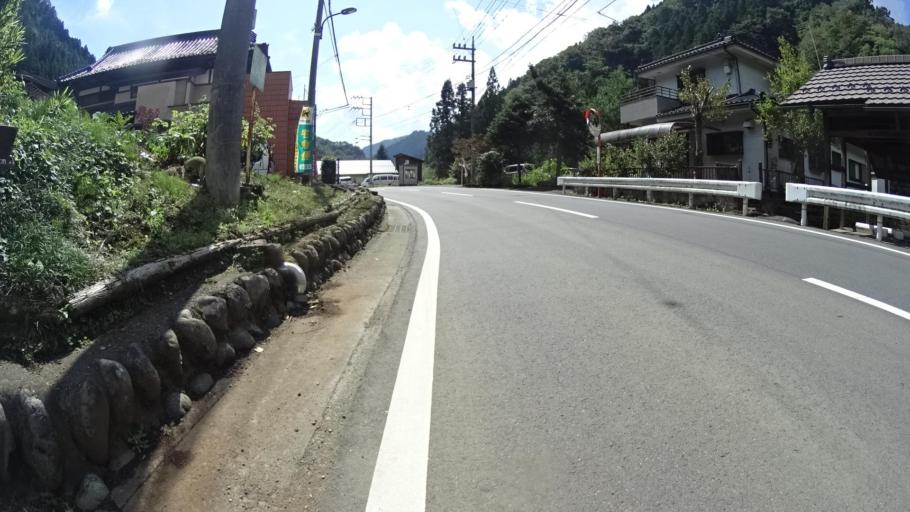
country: JP
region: Tokyo
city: Itsukaichi
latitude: 35.7385
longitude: 139.1435
